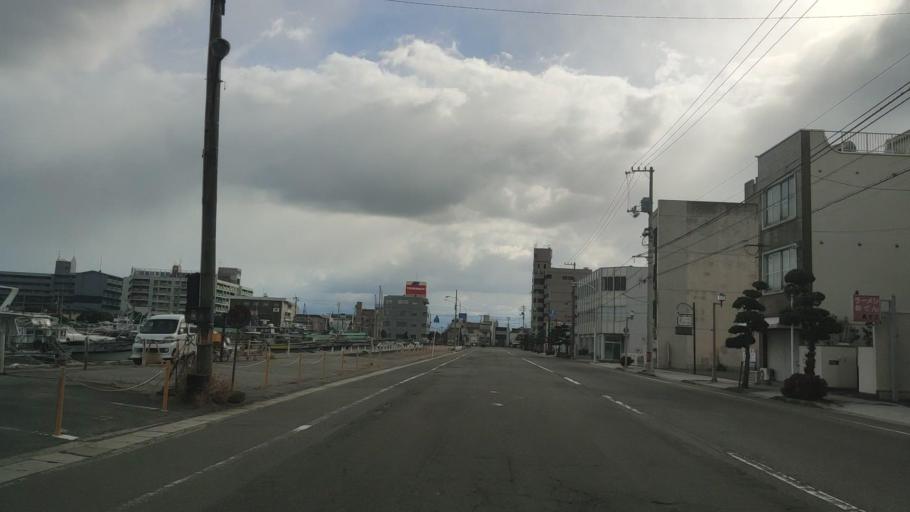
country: JP
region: Ehime
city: Saijo
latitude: 34.0674
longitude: 133.0055
